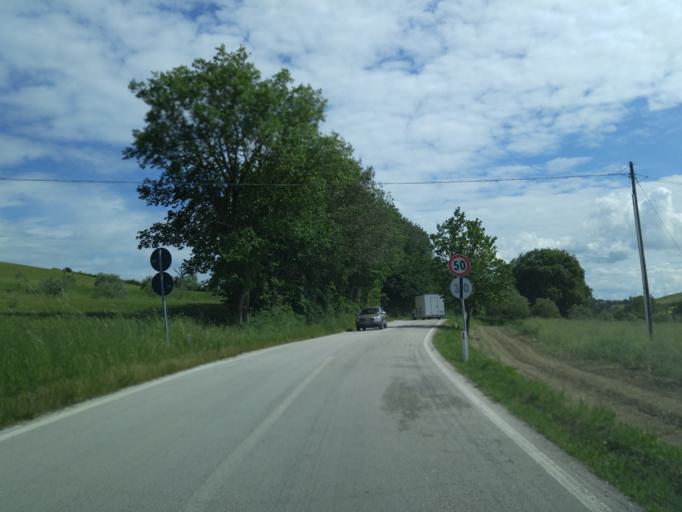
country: IT
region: The Marches
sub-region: Provincia di Pesaro e Urbino
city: Bellocchi
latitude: 43.7893
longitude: 13.0426
